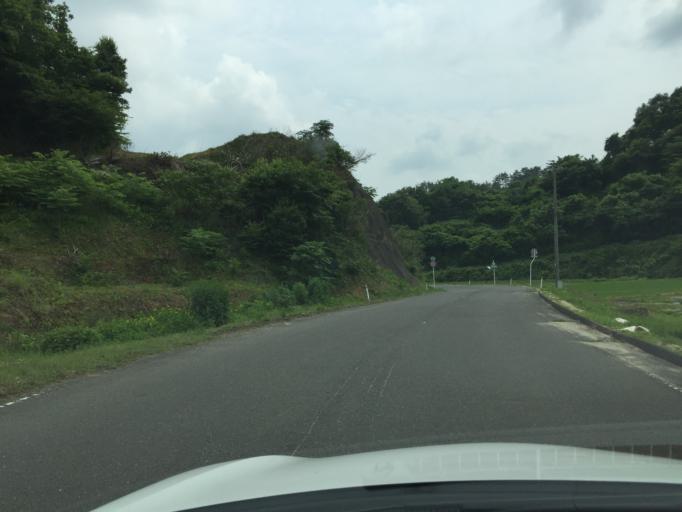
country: JP
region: Fukushima
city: Ishikawa
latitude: 37.2359
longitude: 140.4943
